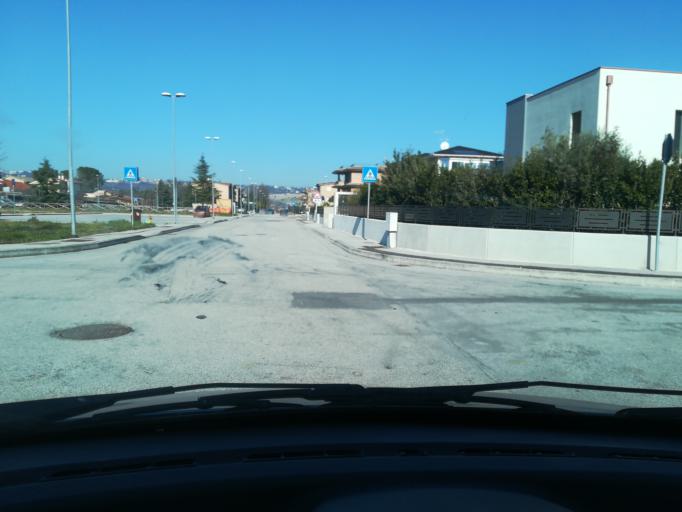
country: IT
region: The Marches
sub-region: Provincia di Macerata
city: Zona Industriale
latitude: 43.2623
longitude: 13.4963
